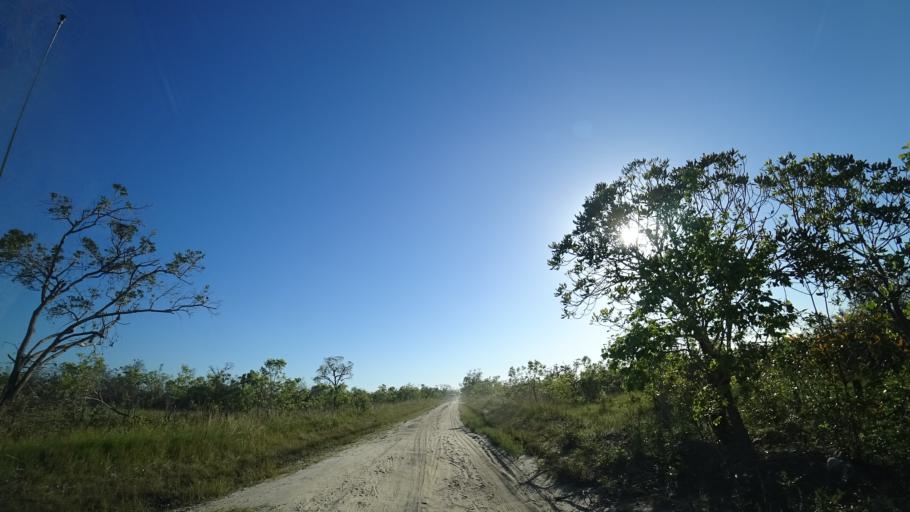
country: MZ
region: Sofala
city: Beira
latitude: -19.5753
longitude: 35.2147
